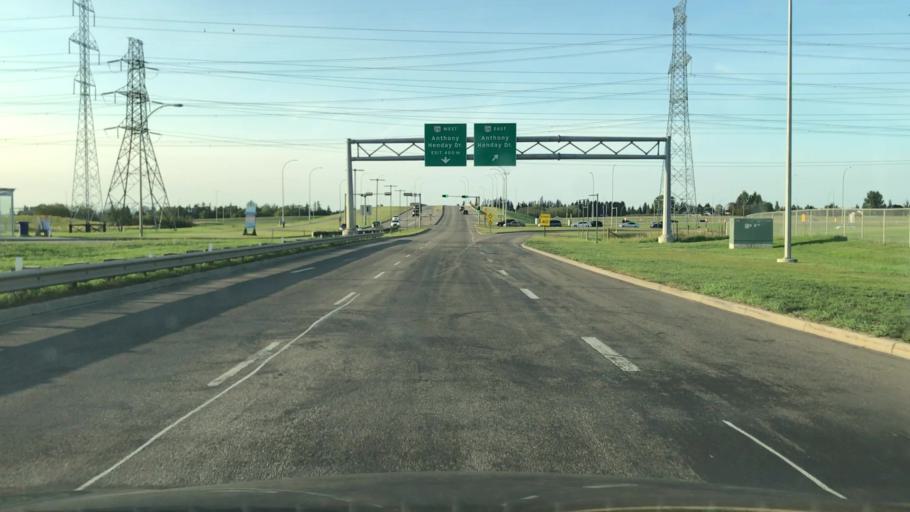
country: CA
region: Alberta
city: Beaumont
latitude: 53.4315
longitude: -113.4177
